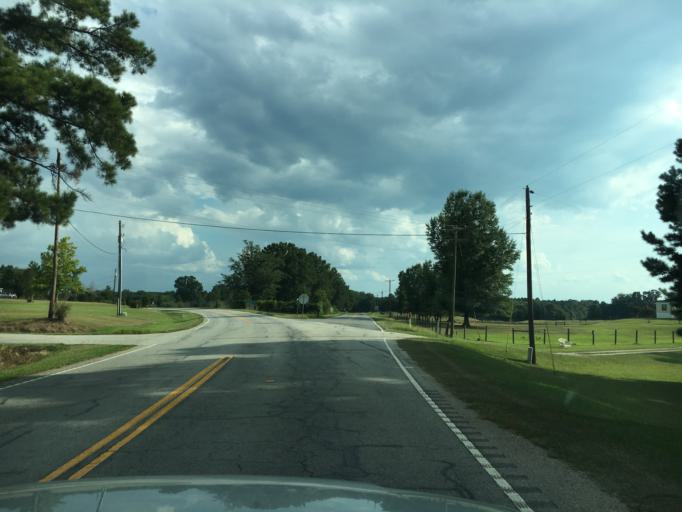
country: US
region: South Carolina
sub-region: Greenwood County
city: Ninety Six
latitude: 34.2178
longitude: -82.0376
